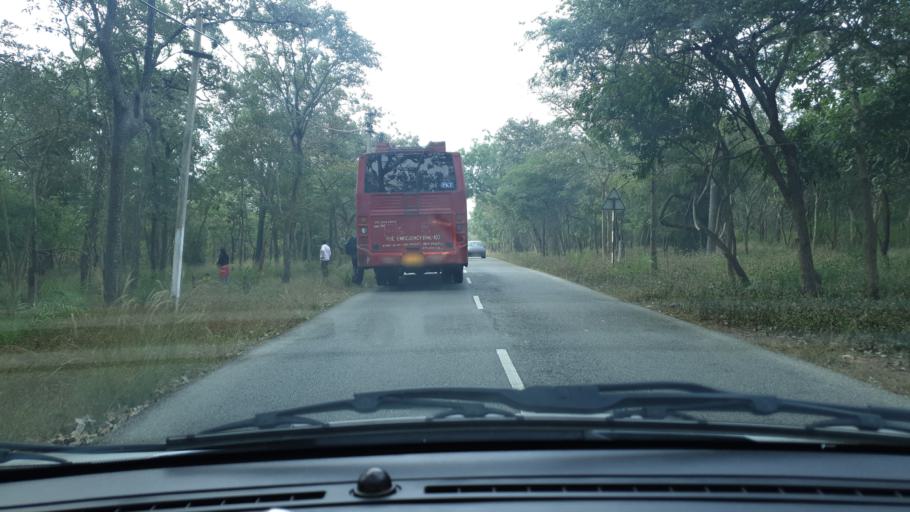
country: IN
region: Andhra Pradesh
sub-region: Kurnool
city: Srisailam
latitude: 16.2910
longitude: 78.7303
